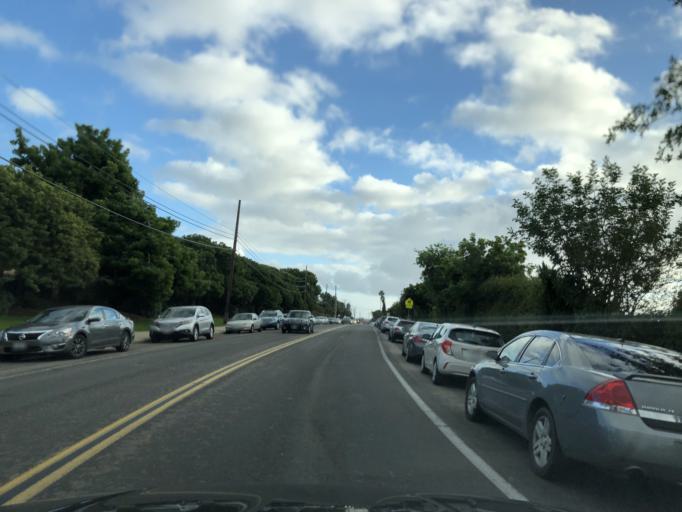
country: US
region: California
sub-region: San Diego County
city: La Jolla
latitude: 32.8157
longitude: -117.1824
